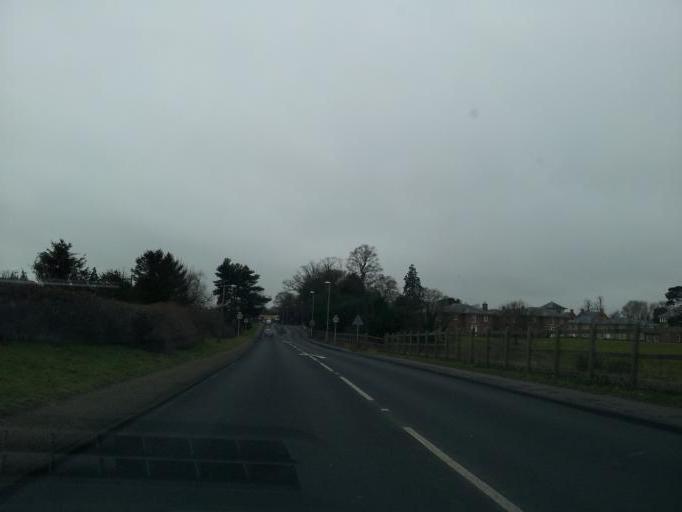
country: GB
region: England
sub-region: Essex
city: Manningtree
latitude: 51.9420
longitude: 1.0460
